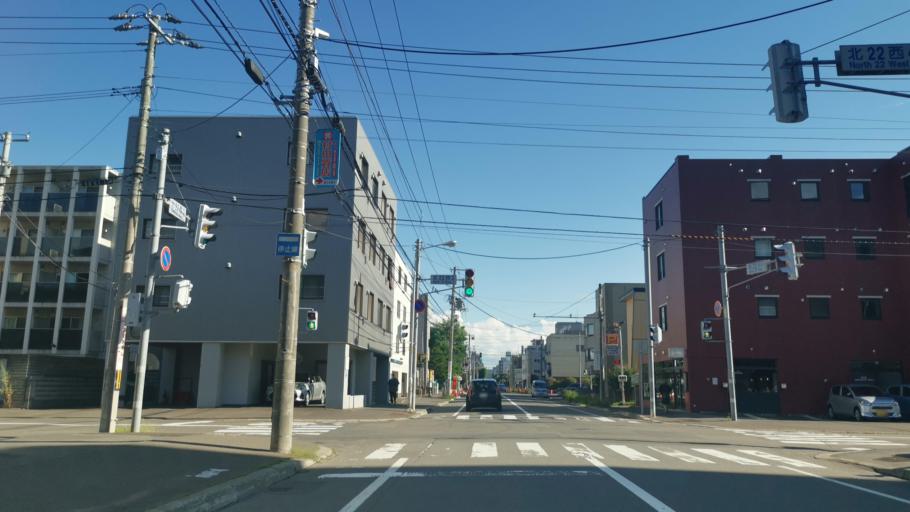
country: JP
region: Hokkaido
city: Sapporo
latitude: 43.0883
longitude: 141.3451
